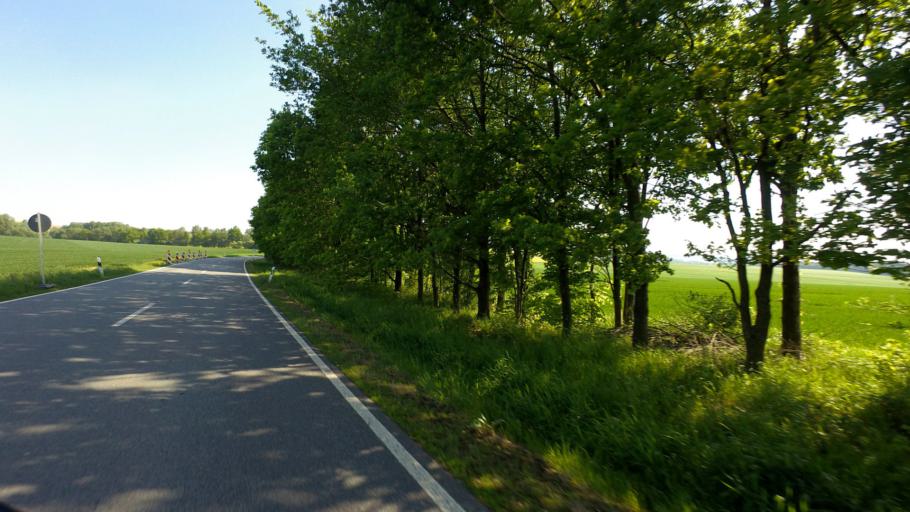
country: DE
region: Saxony
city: Stolpen
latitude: 51.0322
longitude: 14.1312
